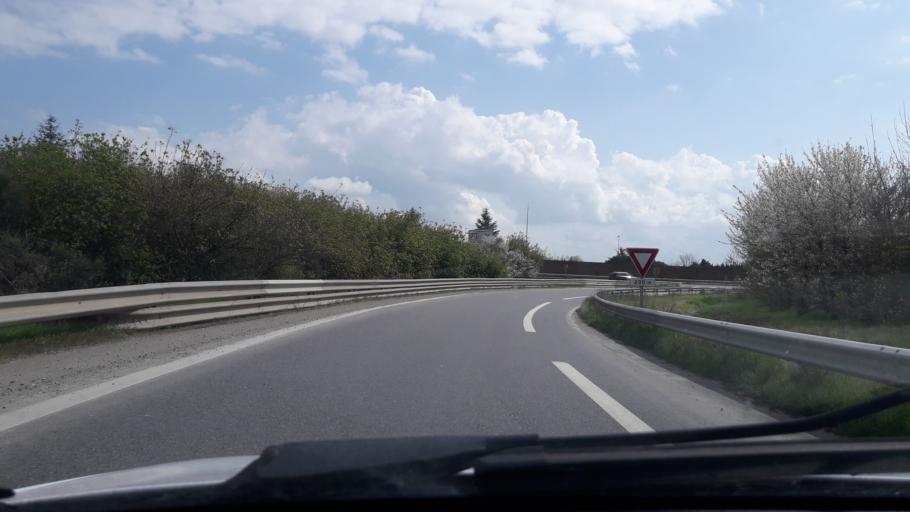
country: FR
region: Midi-Pyrenees
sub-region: Departement de la Haute-Garonne
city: Seysses
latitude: 43.4752
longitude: 1.3186
